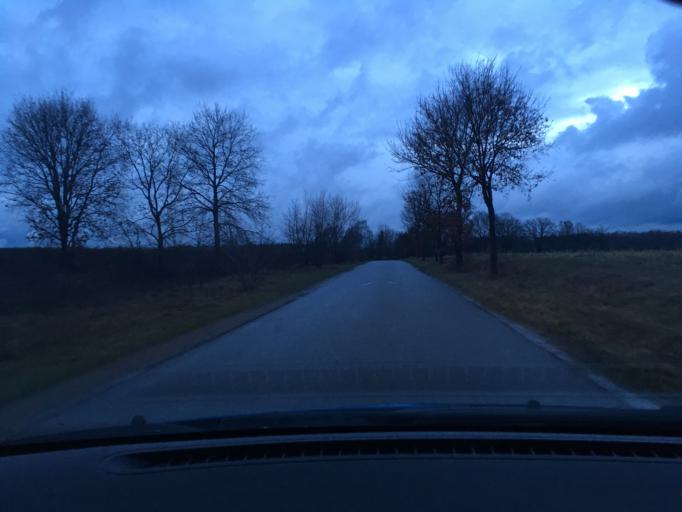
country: DE
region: Lower Saxony
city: Betzendorf
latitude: 53.1414
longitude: 10.3142
